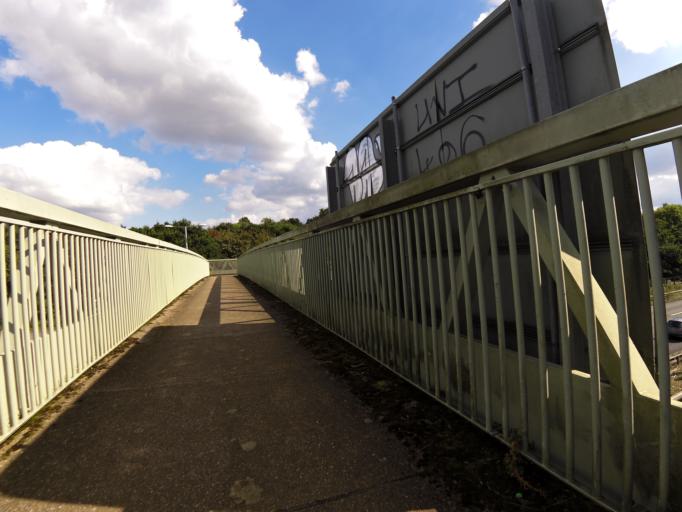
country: GB
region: England
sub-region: Greater London
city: High Barnet
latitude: 51.6727
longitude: -0.2387
